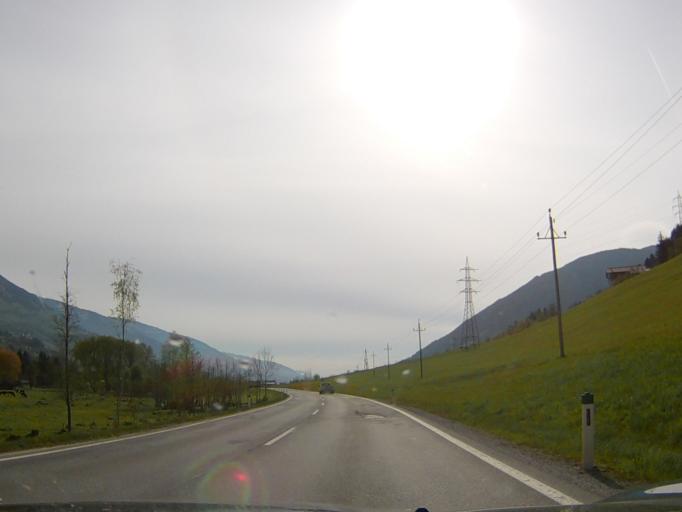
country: AT
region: Salzburg
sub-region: Politischer Bezirk Zell am See
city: Hollersbach im Pinzgau
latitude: 47.2765
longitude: 12.4482
